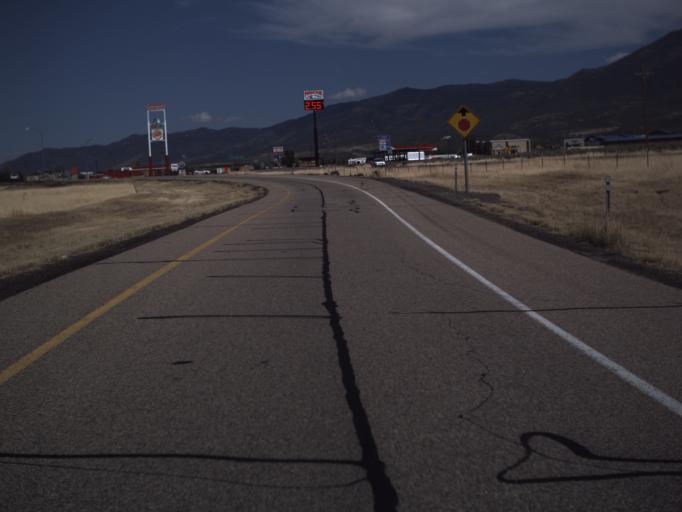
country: US
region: Utah
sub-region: Millard County
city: Fillmore
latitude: 38.9457
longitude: -112.3505
